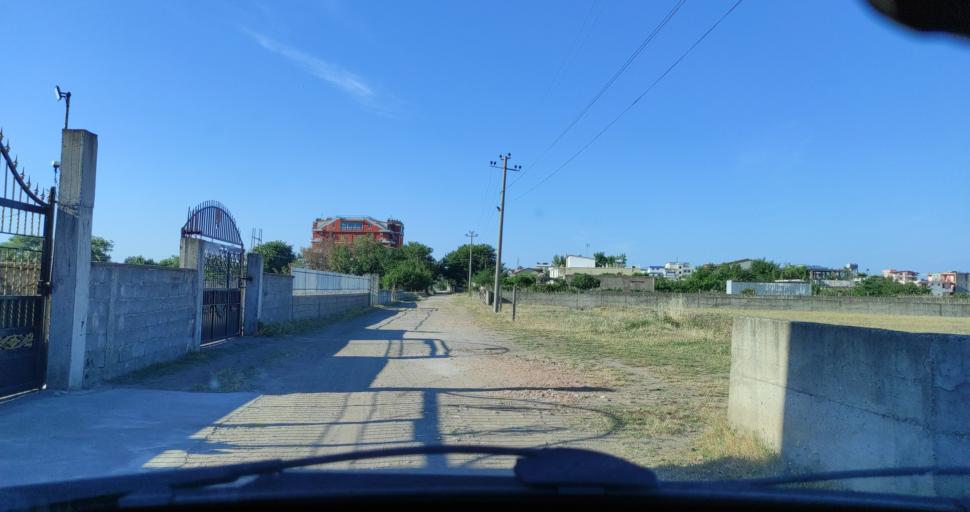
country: AL
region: Shkoder
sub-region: Rrethi i Shkodres
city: Velipoje
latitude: 41.8707
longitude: 19.4260
